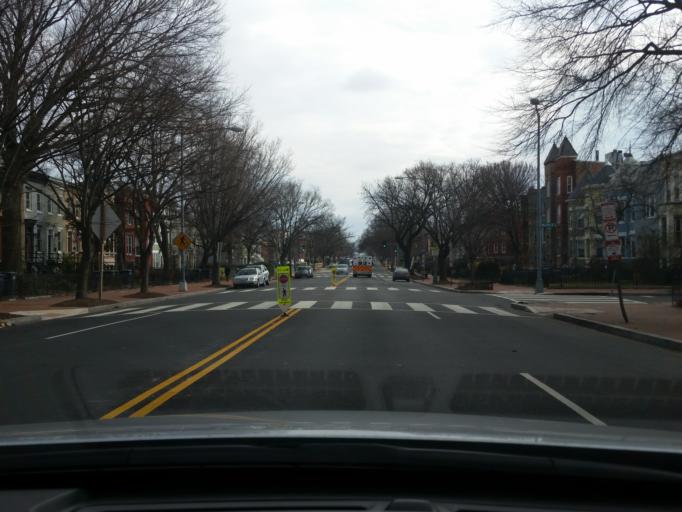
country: US
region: Washington, D.C.
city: Washington, D.C.
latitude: 38.9122
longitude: -77.0173
